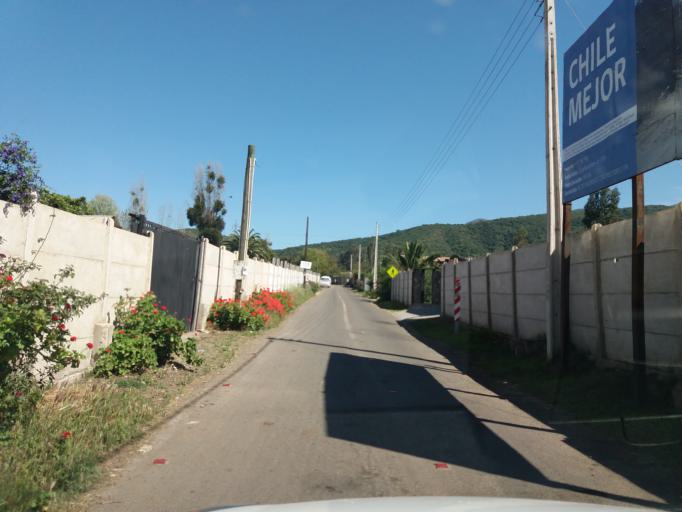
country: CL
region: Valparaiso
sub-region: Provincia de Quillota
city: Quillota
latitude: -32.8591
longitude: -71.2669
